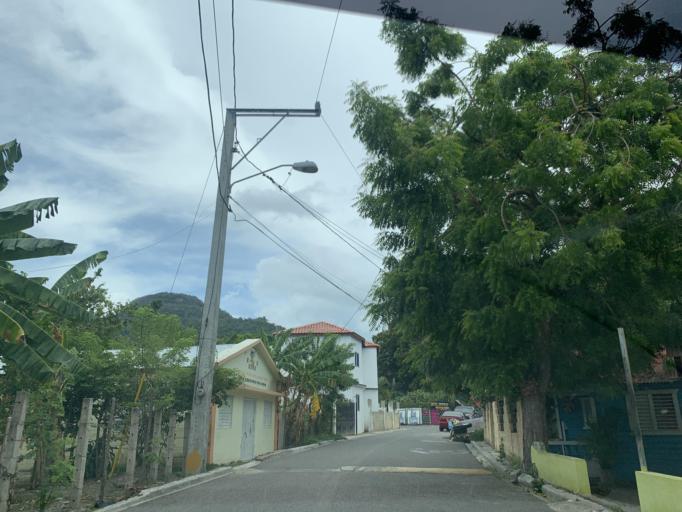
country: DO
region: Puerto Plata
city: Imbert
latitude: 19.8241
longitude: -70.7768
